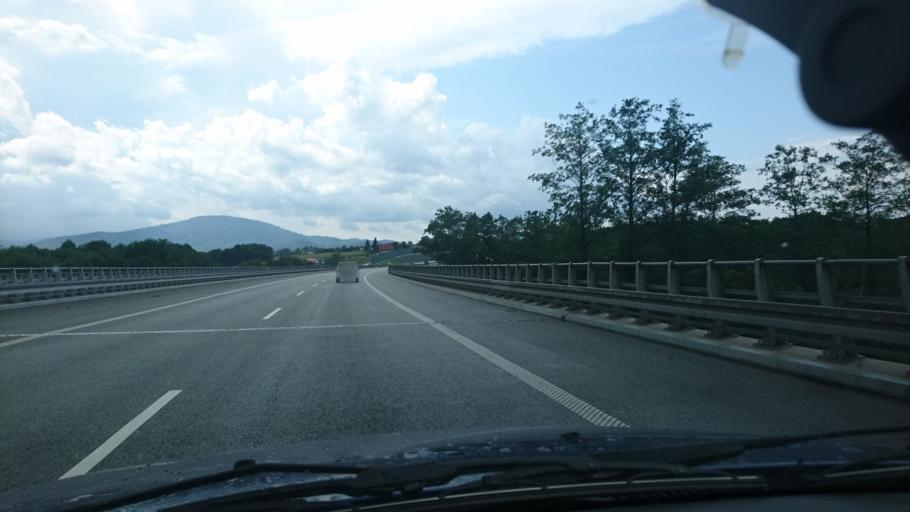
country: PL
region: Silesian Voivodeship
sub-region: Powiat zywiecki
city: Pietrzykowice
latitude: 49.6850
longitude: 19.1478
